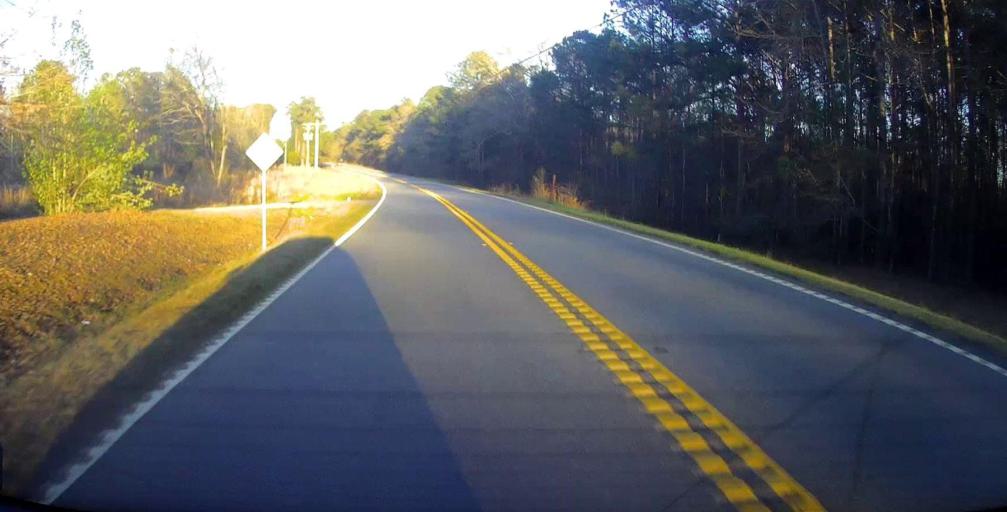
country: US
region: Alabama
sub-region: Lee County
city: Smiths Station
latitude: 32.6536
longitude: -85.0058
